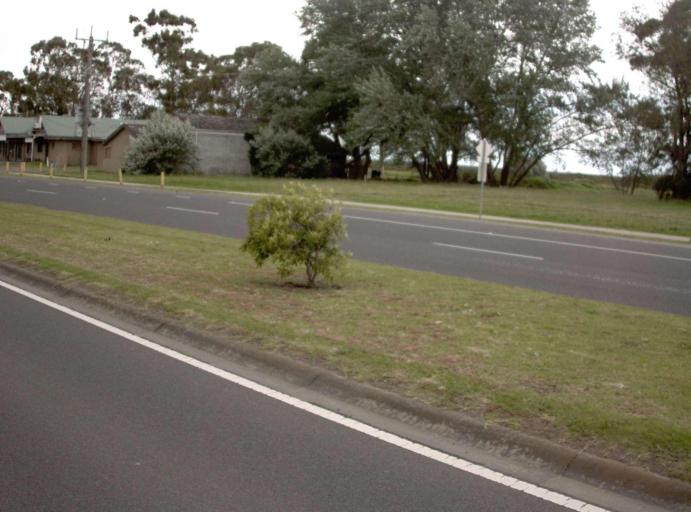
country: AU
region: Victoria
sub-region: Casey
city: Tooradin
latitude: -38.2113
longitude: 145.3778
